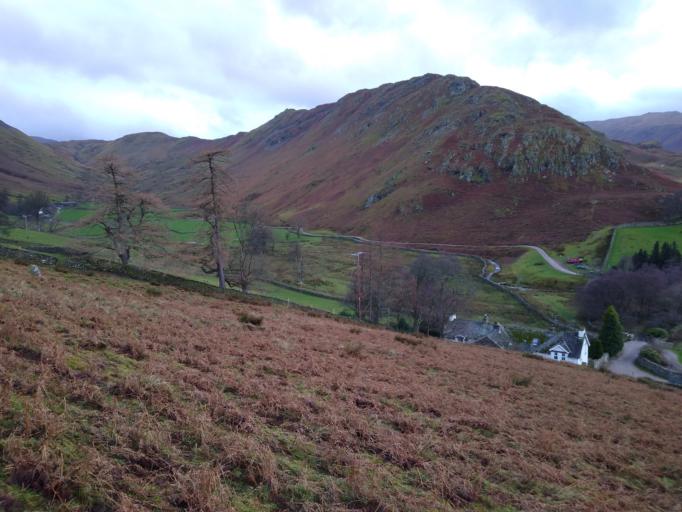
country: GB
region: England
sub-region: Cumbria
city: Penrith
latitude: 54.5683
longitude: -2.8578
